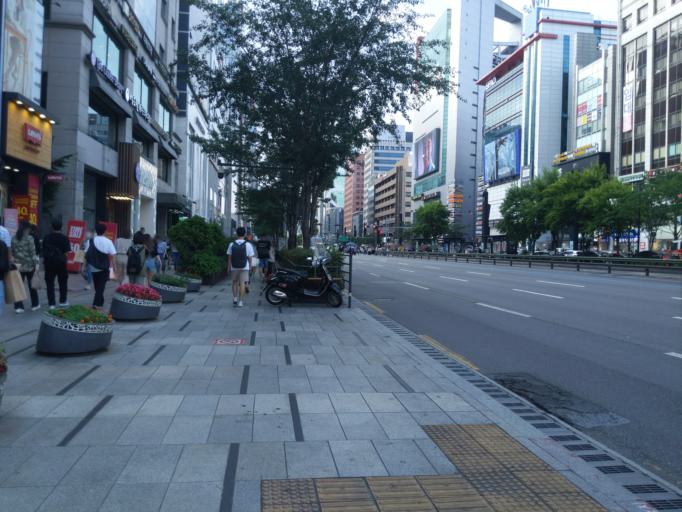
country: KR
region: Seoul
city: Seoul
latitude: 37.5000
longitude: 127.0266
